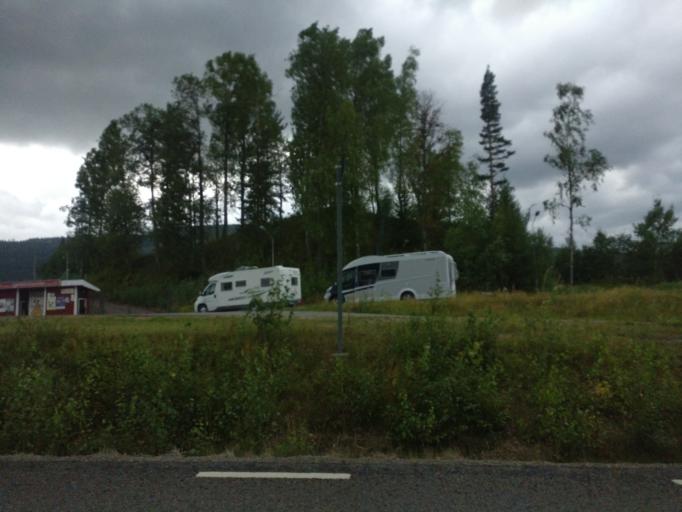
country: SE
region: Vaermland
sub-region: Torsby Kommun
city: Torsby
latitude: 60.7351
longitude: 12.8655
